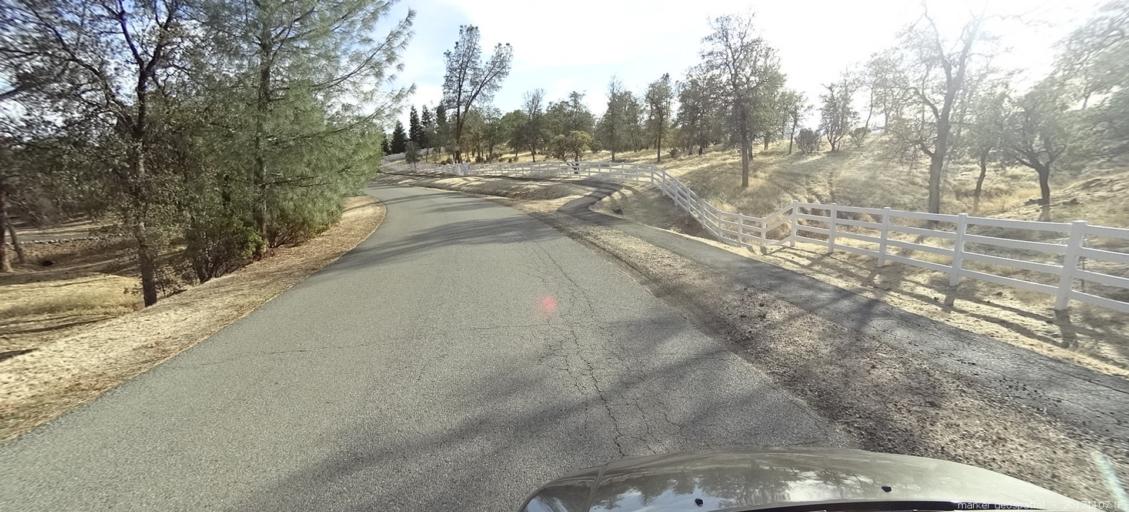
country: US
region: California
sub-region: Shasta County
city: Shasta
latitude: 40.5100
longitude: -122.4741
